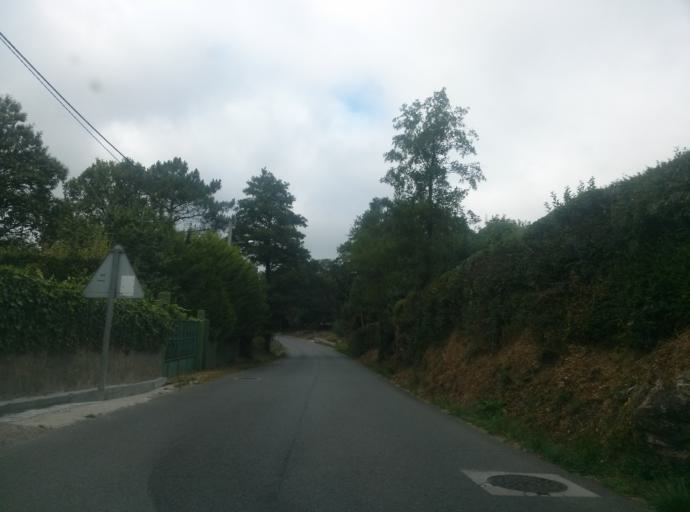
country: ES
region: Galicia
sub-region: Provincia de Lugo
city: Lugo
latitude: 43.0540
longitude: -7.5649
